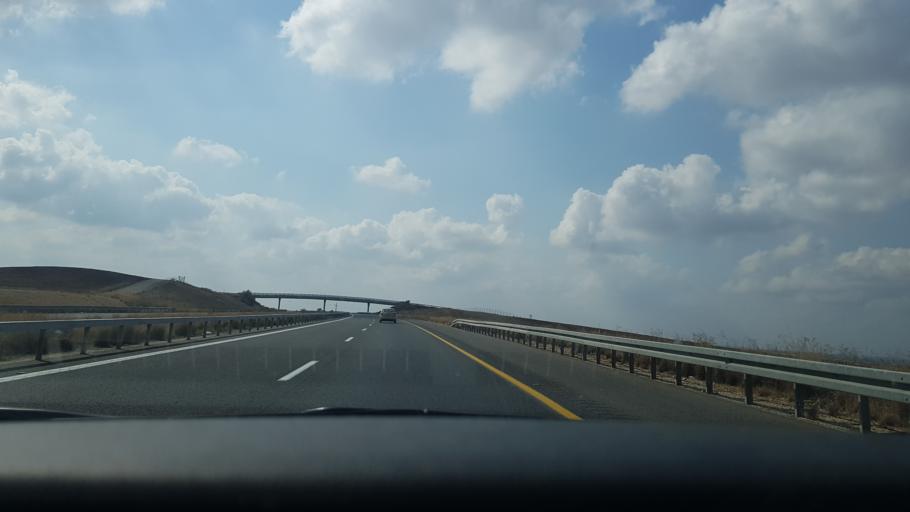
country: IL
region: Southern District
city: Qiryat Gat
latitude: 31.6805
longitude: 34.8072
